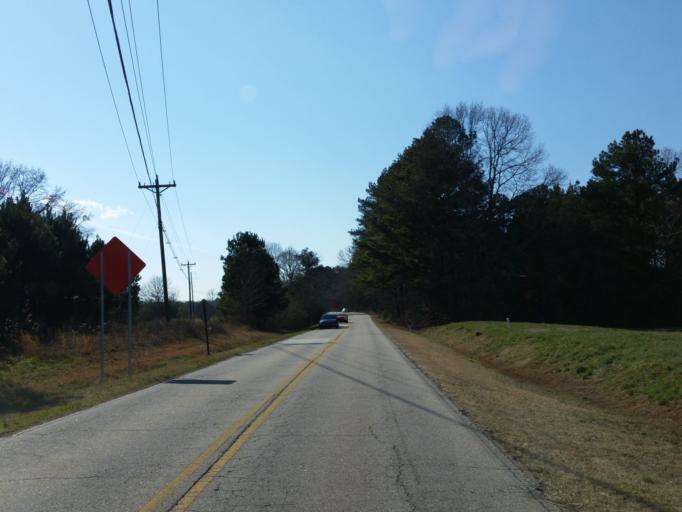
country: US
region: Georgia
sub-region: Henry County
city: McDonough
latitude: 33.4476
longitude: -84.2157
